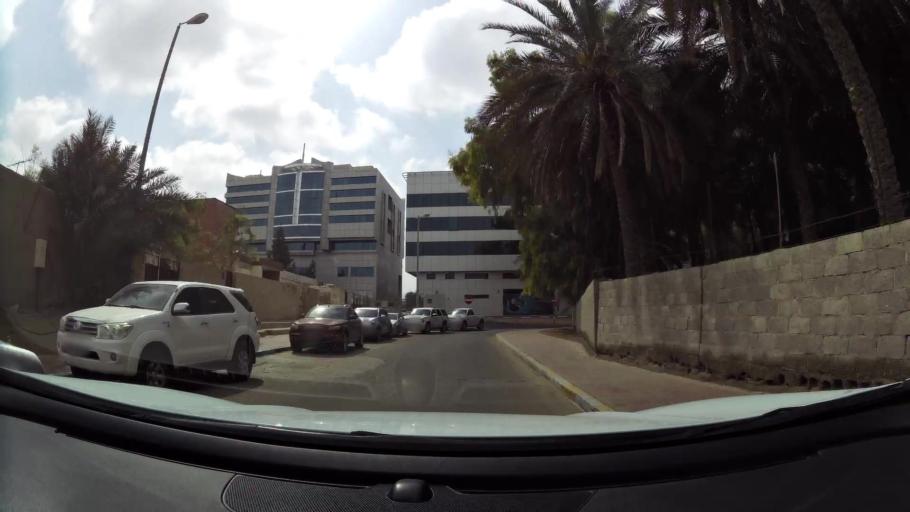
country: AE
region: Abu Dhabi
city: Al Ain
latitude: 24.2289
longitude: 55.7617
